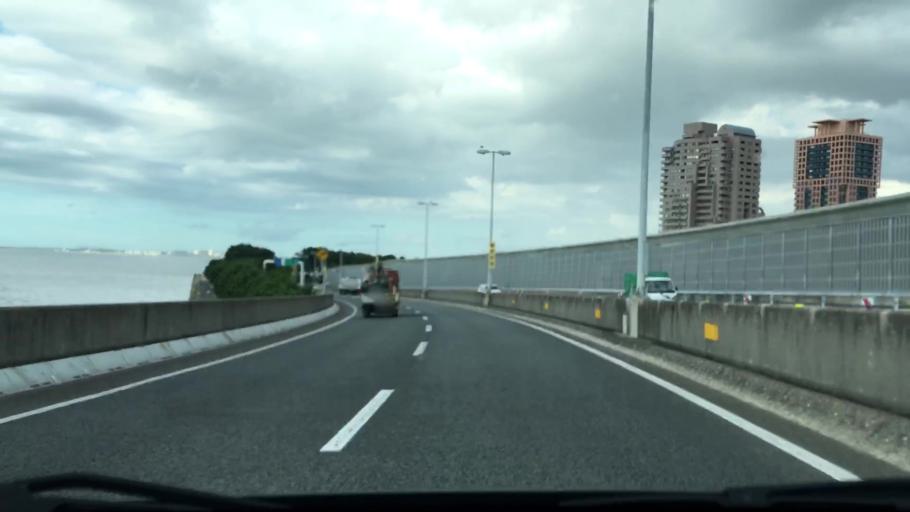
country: JP
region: Fukuoka
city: Fukuoka-shi
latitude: 33.5899
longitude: 130.3451
